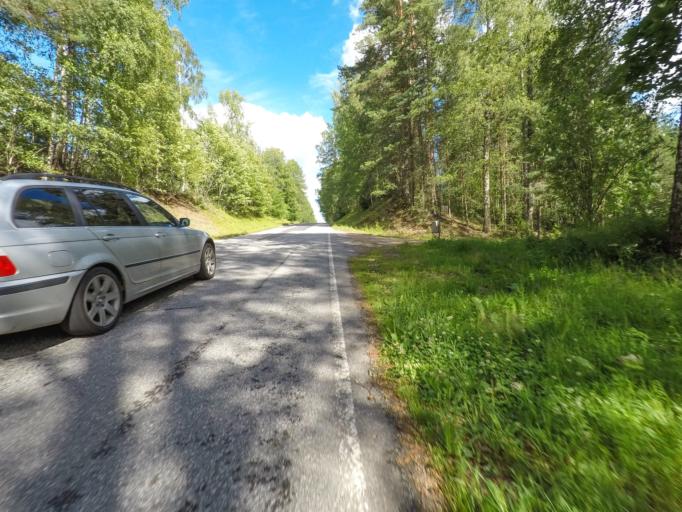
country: FI
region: South Karelia
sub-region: Lappeenranta
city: Joutseno
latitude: 61.1257
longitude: 28.3951
